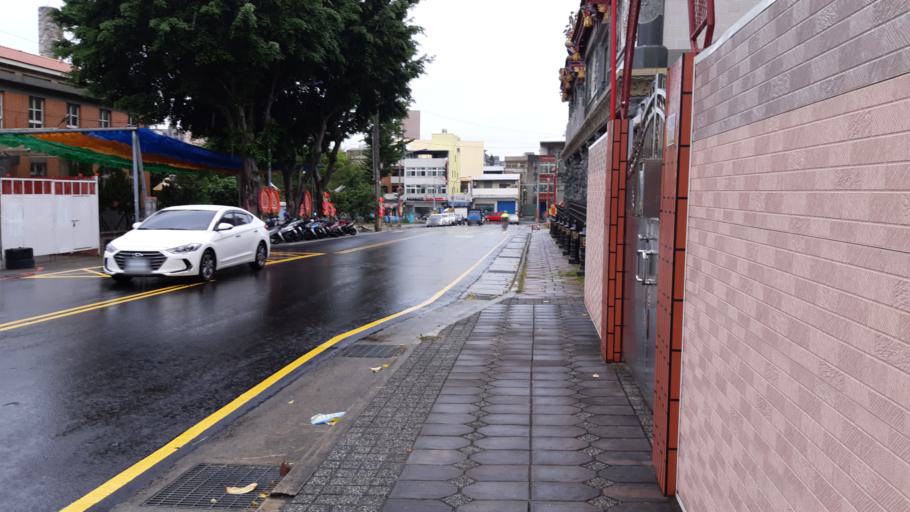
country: TW
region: Taiwan
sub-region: Hsinchu
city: Hsinchu
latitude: 24.7992
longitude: 120.9588
